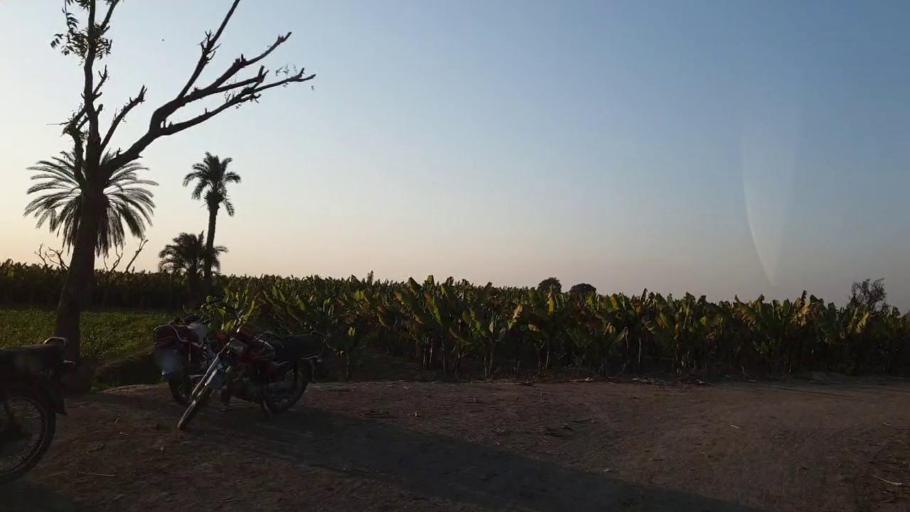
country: PK
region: Sindh
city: Tando Jam
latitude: 25.4833
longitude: 68.6021
